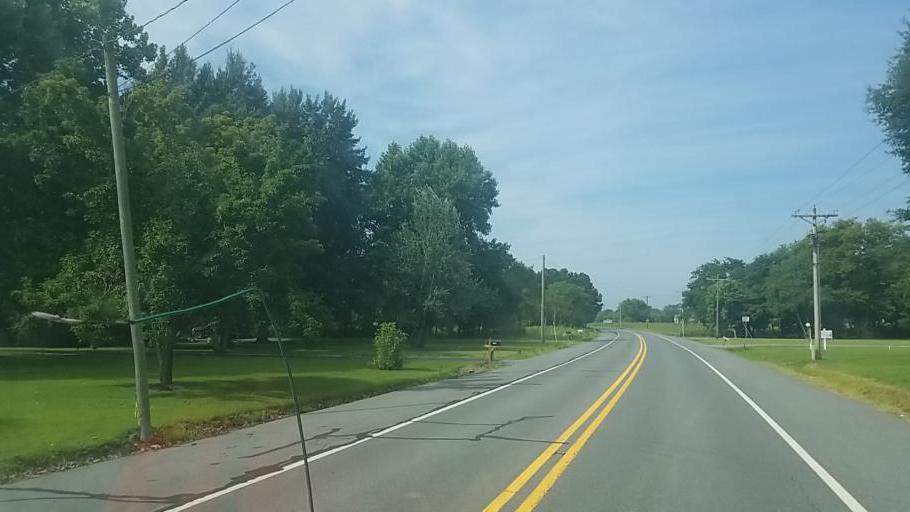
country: US
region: Delaware
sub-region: Sussex County
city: Long Neck
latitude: 38.5428
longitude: -75.1780
